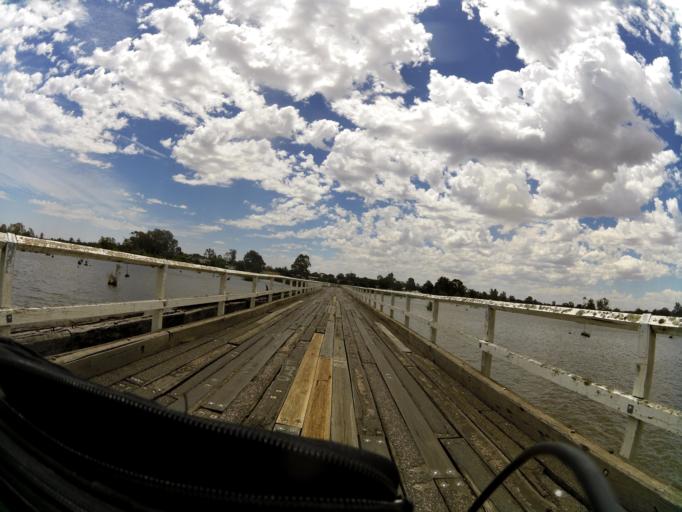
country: AU
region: Victoria
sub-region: Campaspe
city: Kyabram
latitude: -36.7467
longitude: 145.1400
